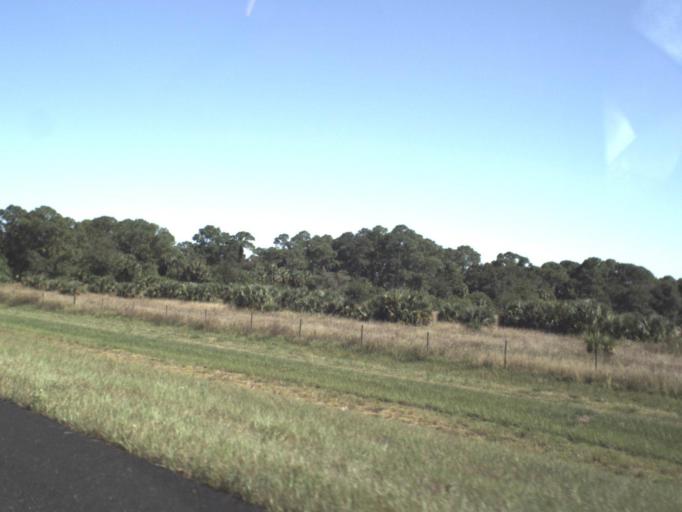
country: US
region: Florida
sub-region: Hendry County
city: Port LaBelle
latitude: 26.7640
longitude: -81.3845
